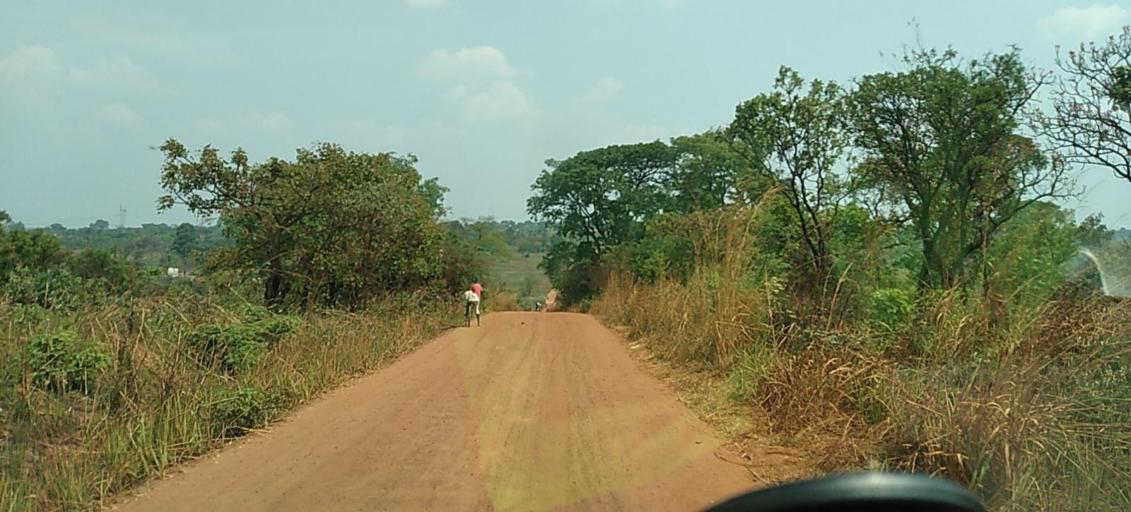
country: ZM
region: North-Western
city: Kansanshi
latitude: -12.1091
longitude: 26.3663
